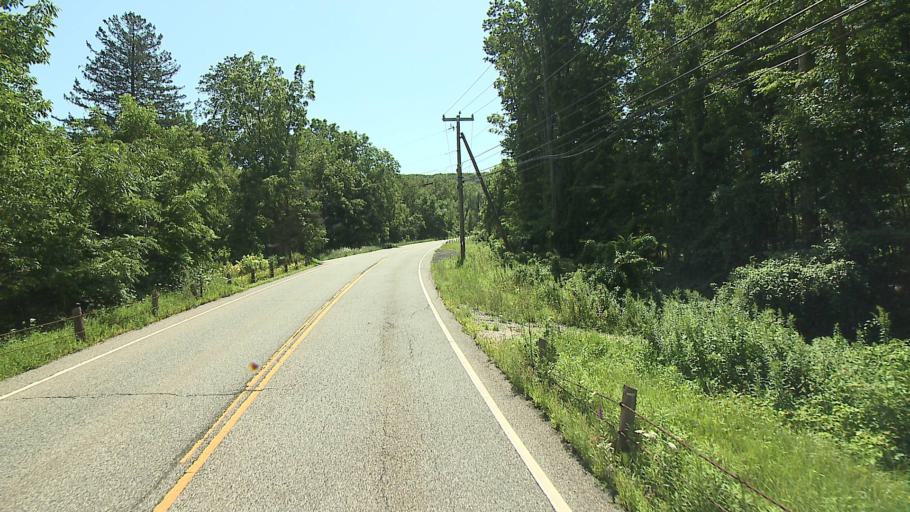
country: US
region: Connecticut
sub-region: Litchfield County
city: Kent
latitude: 41.8525
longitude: -73.4424
